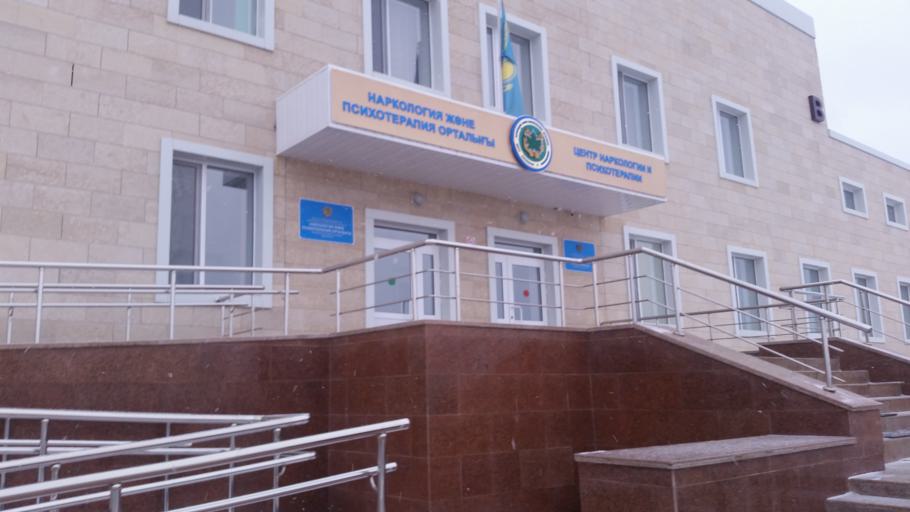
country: KZ
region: Astana Qalasy
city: Astana
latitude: 51.0817
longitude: 71.4142
